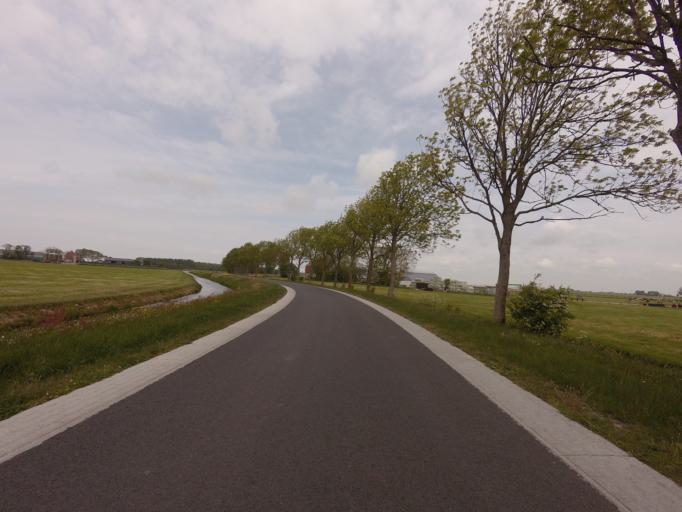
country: NL
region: Friesland
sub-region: Sudwest Fryslan
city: Bolsward
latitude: 53.0875
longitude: 5.4835
